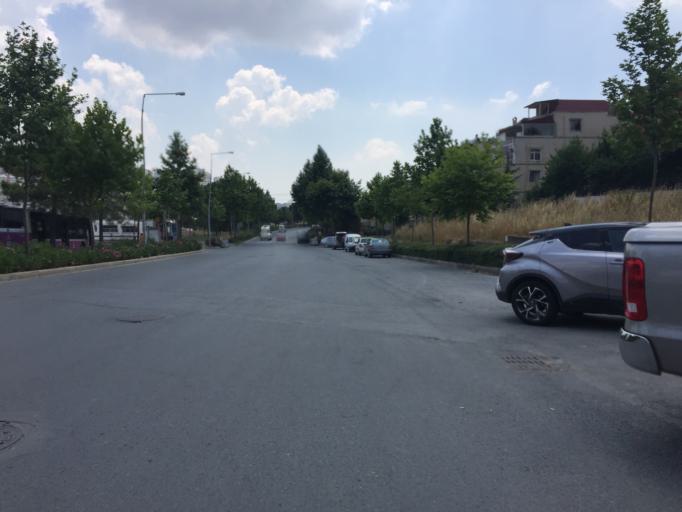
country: TR
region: Istanbul
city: Esenyurt
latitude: 41.0844
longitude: 28.6748
